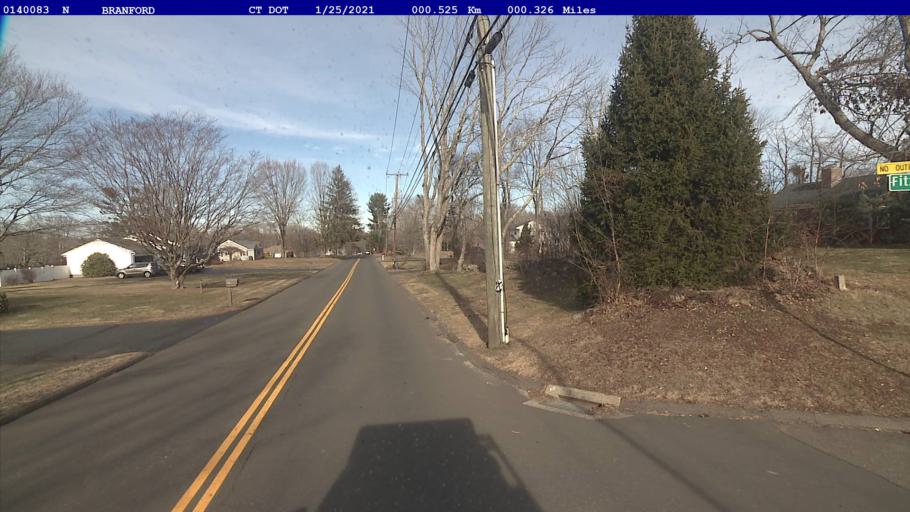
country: US
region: Connecticut
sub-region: New Haven County
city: North Branford
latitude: 41.2900
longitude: -72.7766
